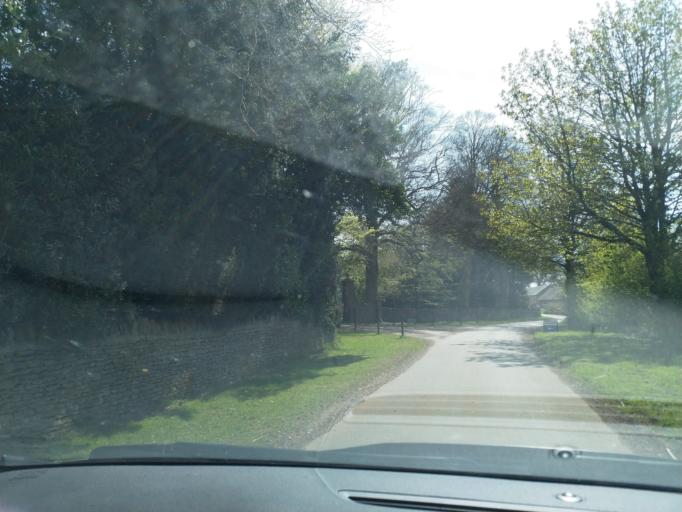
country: GB
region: England
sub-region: Oxfordshire
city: Adderbury
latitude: 52.0739
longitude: -1.2420
